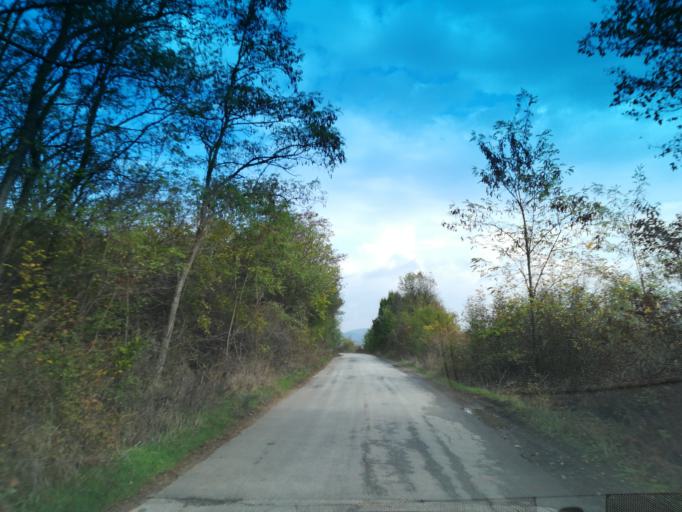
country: BG
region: Stara Zagora
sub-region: Obshtina Nikolaevo
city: Elkhovo
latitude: 42.3313
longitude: 25.4039
